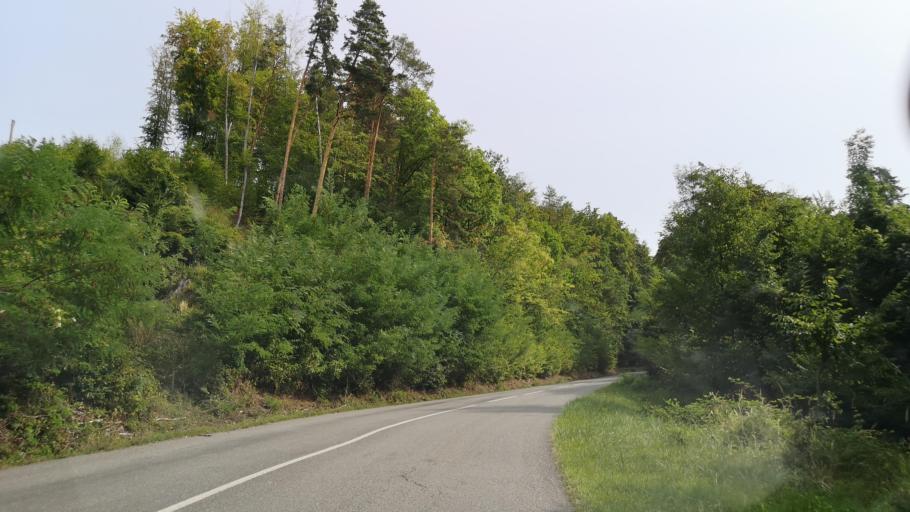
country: SK
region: Banskobystricky
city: Tisovec
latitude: 48.5672
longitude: 20.0260
